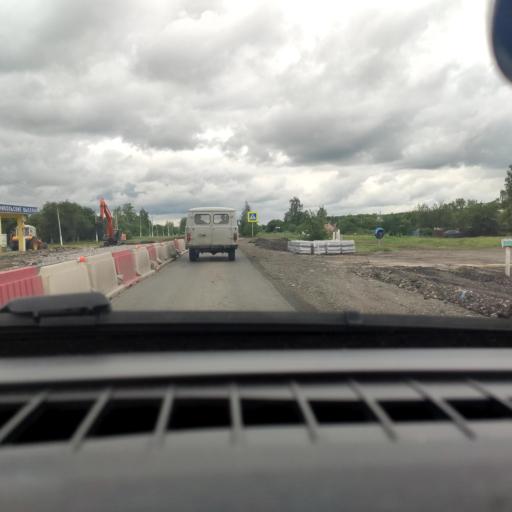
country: RU
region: Lipetsk
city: Usman'
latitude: 51.9521
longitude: 39.7826
